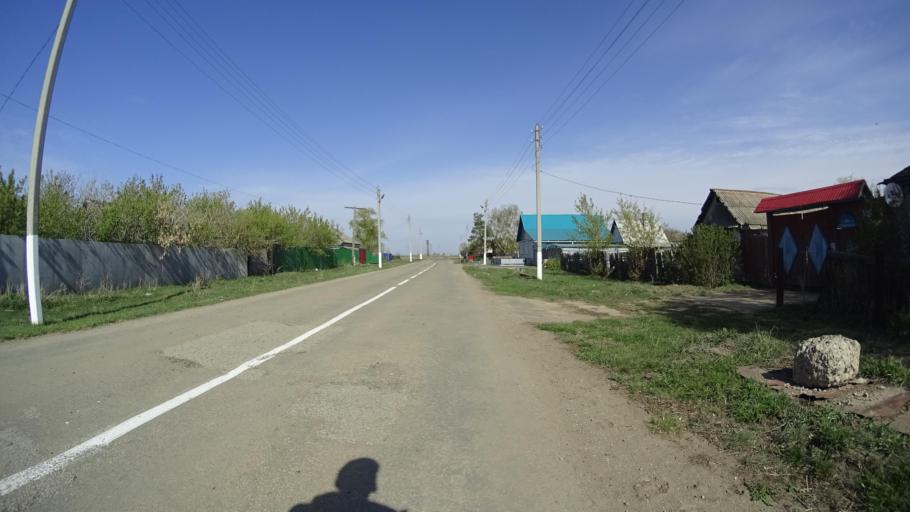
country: RU
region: Chelyabinsk
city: Chesma
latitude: 53.8018
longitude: 61.0188
